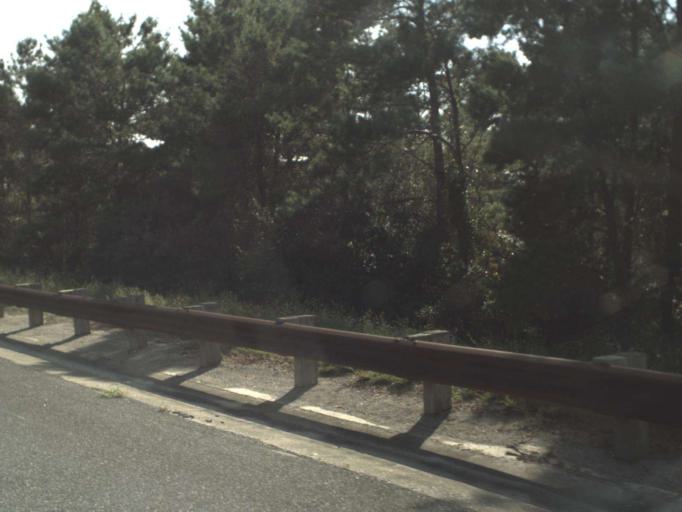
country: US
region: Florida
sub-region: Gulf County
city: Port Saint Joe
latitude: 29.8736
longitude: -85.3395
